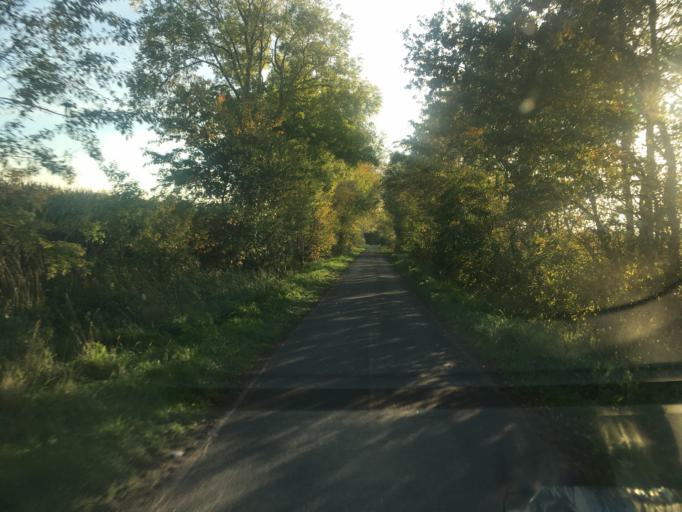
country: DE
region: Schleswig-Holstein
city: Bramstedtlund
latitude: 54.8600
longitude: 9.0774
